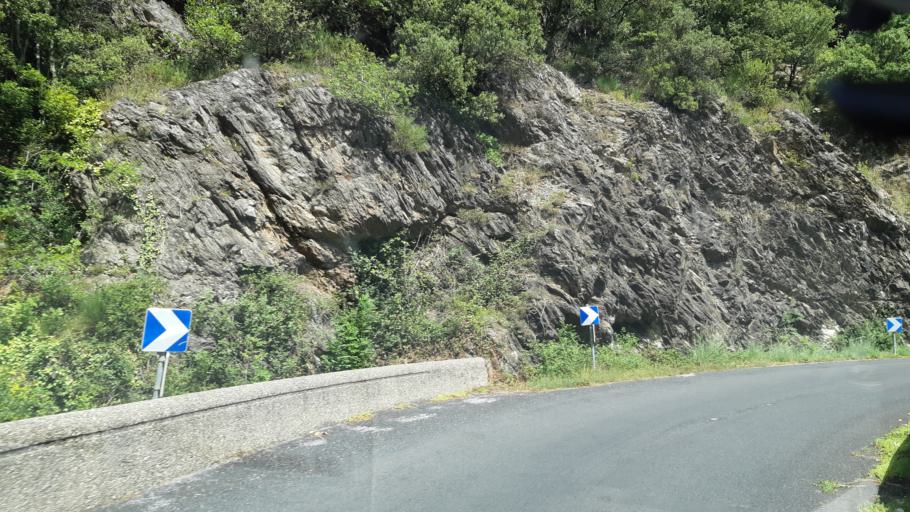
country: FR
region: Languedoc-Roussillon
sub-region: Departement des Pyrenees-Orientales
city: els Banys d'Arles
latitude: 42.5113
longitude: 2.6303
